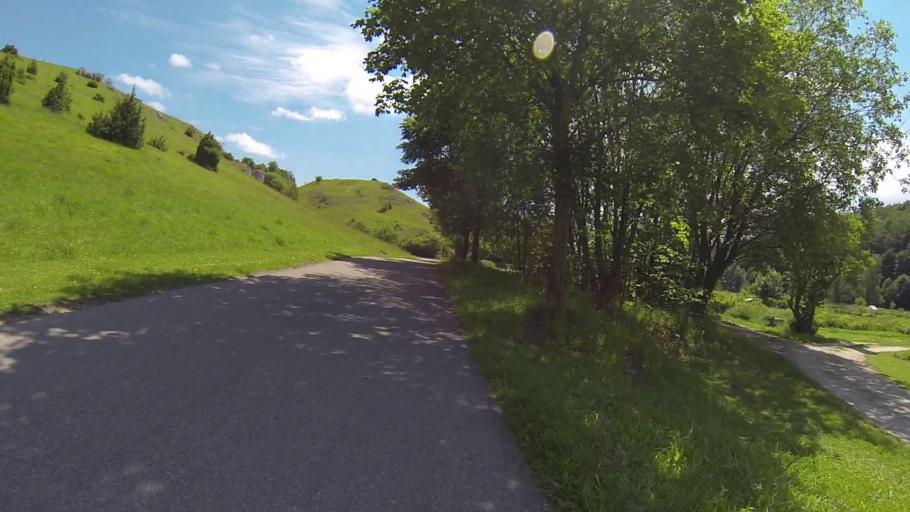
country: DE
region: Baden-Wuerttemberg
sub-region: Regierungsbezirk Stuttgart
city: Herbrechtingen
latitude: 48.6134
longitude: 10.1775
